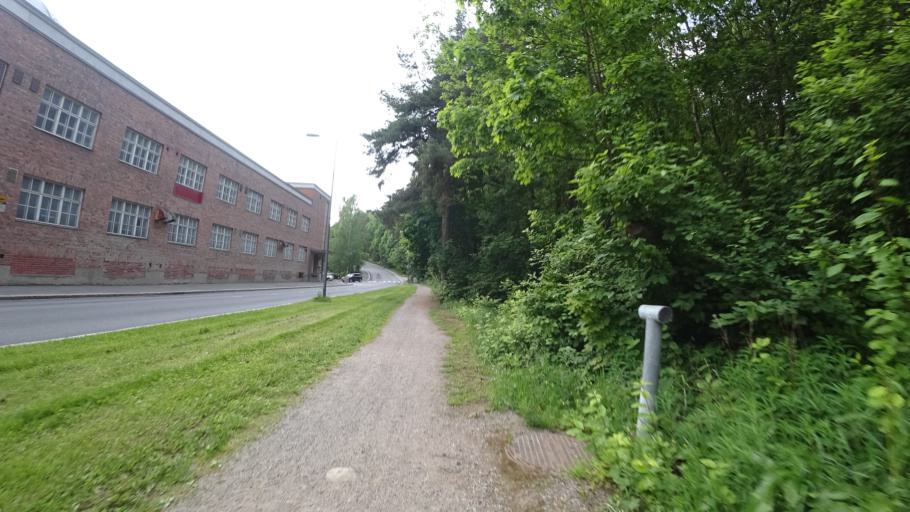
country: FI
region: Pirkanmaa
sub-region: Tampere
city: Tampere
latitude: 61.4938
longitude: 23.7240
